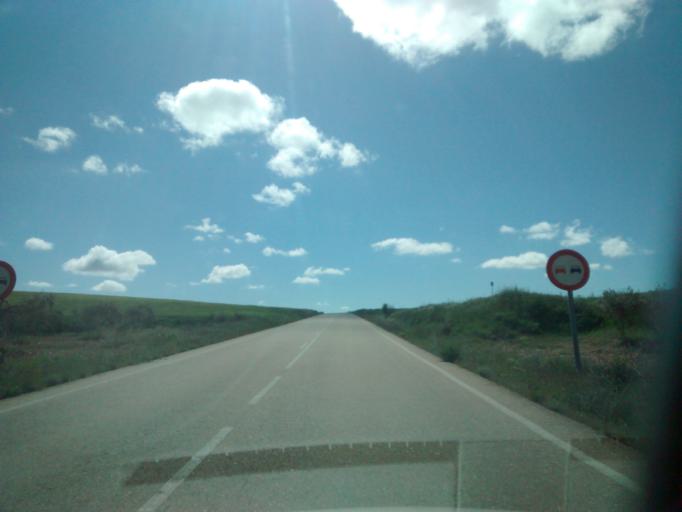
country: ES
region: Aragon
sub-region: Provincia de Zaragoza
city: Perdiguera
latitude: 41.8008
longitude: -0.6788
